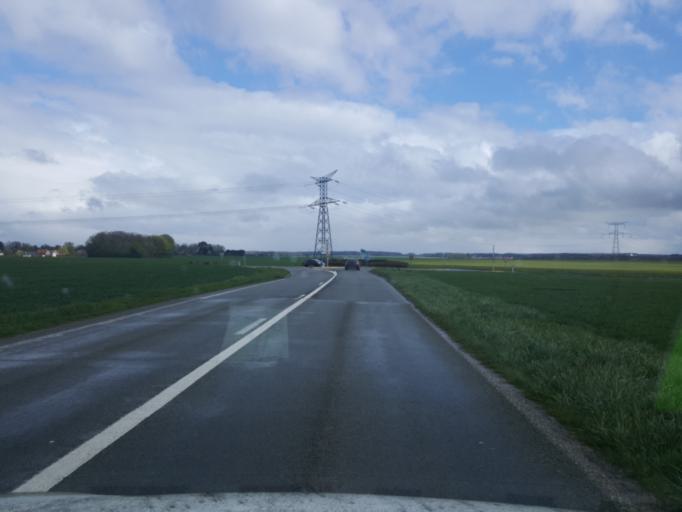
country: FR
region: Picardie
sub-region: Departement de l'Oise
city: Chaumont-en-Vexin
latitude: 49.3160
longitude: 1.8848
